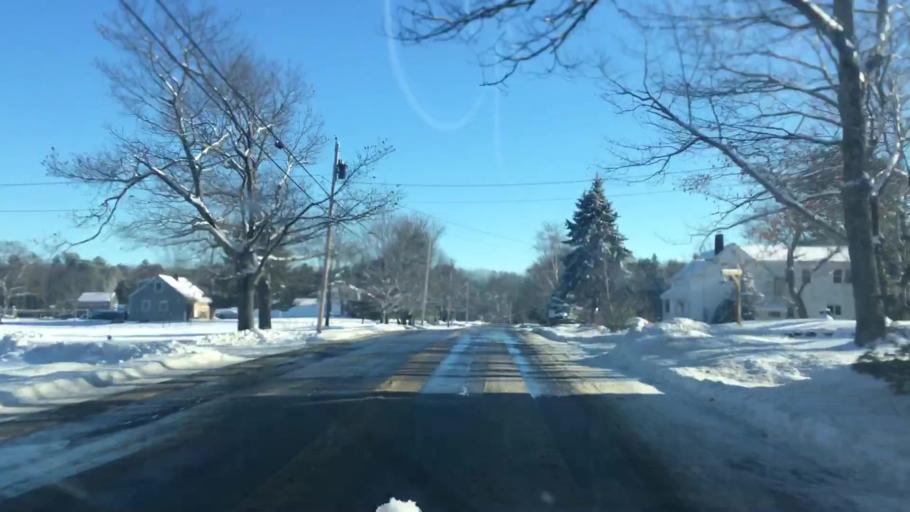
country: US
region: Maine
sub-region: Androscoggin County
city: Lisbon Falls
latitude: 43.9304
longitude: -70.0519
